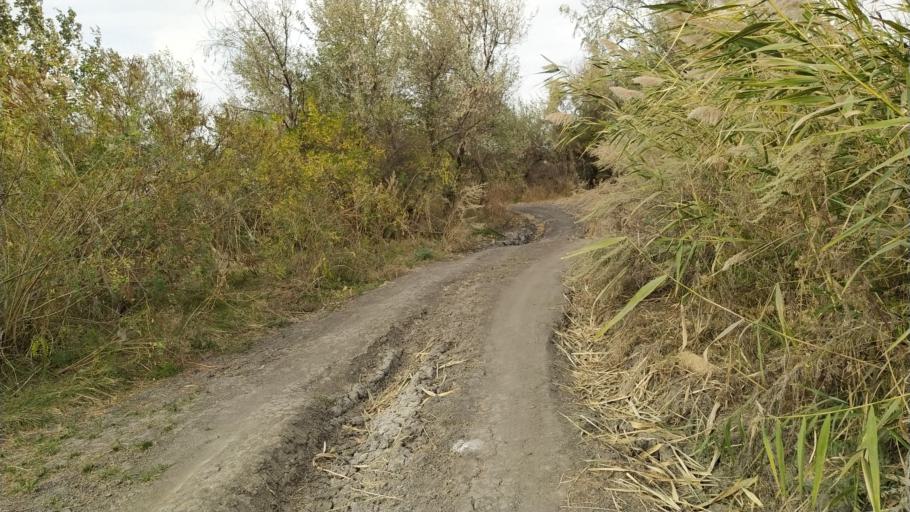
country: RU
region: Rostov
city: Kuleshovka
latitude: 47.1463
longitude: 39.5863
